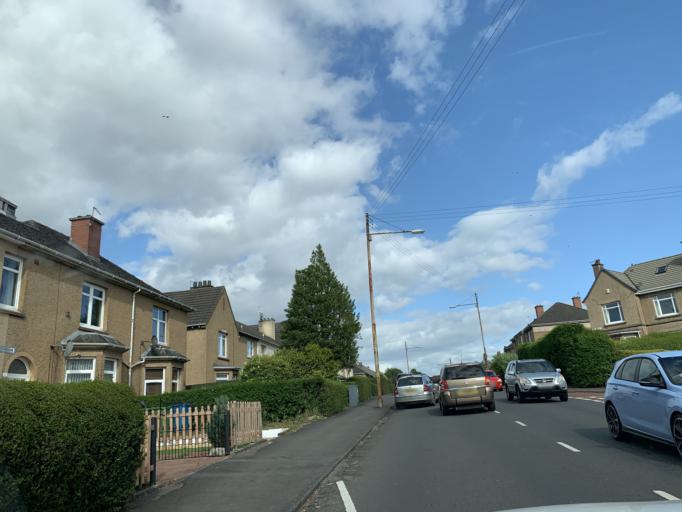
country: GB
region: Scotland
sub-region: Renfrewshire
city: Renfrew
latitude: 55.8515
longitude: -4.3451
